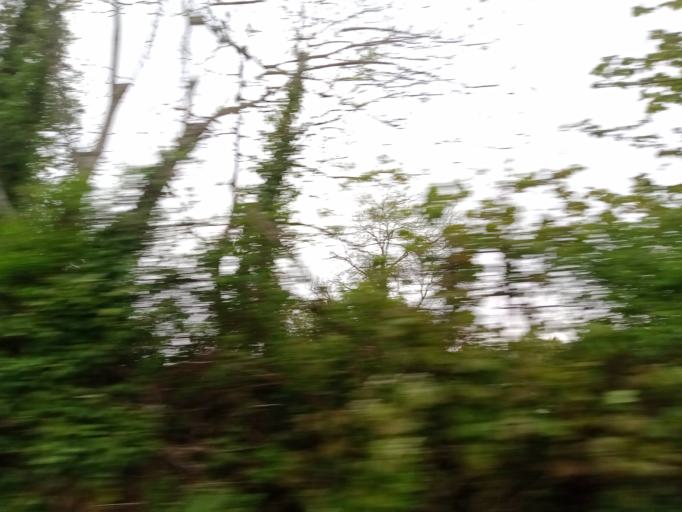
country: IE
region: Leinster
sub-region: Kilkenny
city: Ballyragget
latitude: 52.7188
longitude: -7.4803
